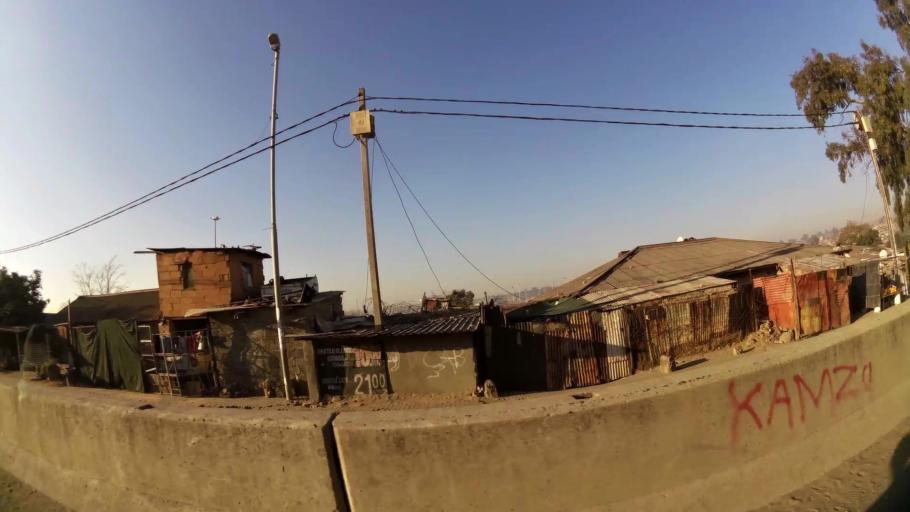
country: ZA
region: Gauteng
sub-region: City of Johannesburg Metropolitan Municipality
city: Modderfontein
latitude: -26.0974
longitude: 28.0984
